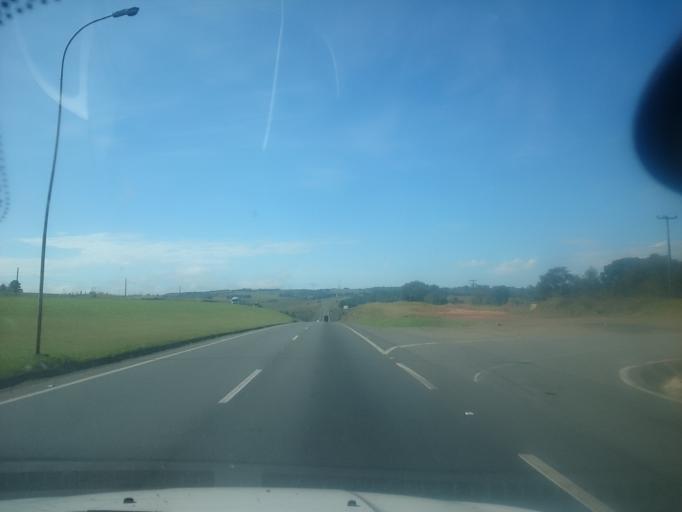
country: BR
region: Parana
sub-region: Campo Largo
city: Campo Largo
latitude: -25.4733
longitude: -49.6996
